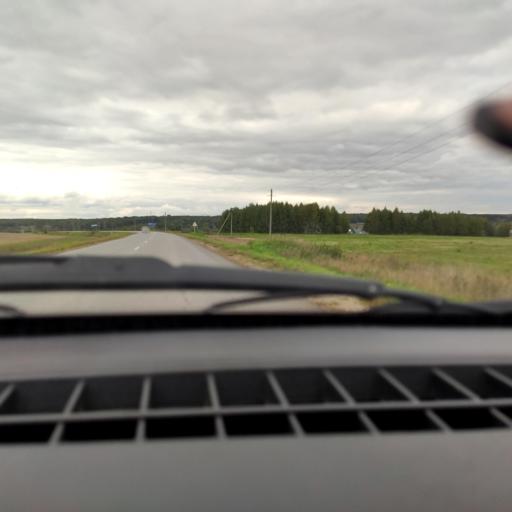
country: RU
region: Bashkortostan
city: Iglino
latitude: 54.7510
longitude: 56.4003
